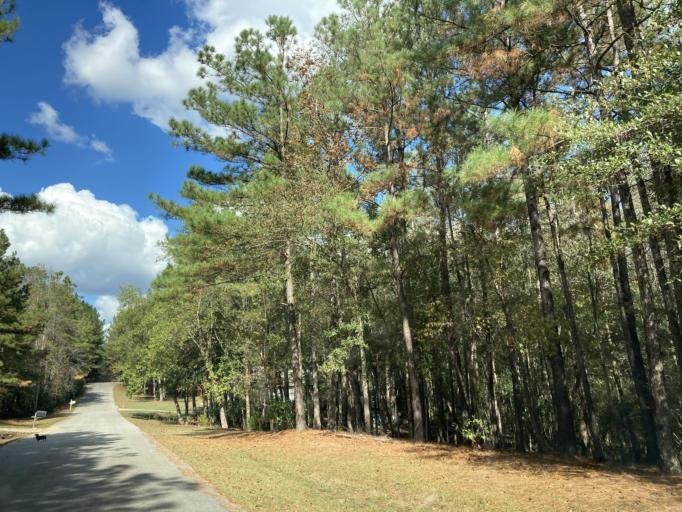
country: US
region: Mississippi
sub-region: Lamar County
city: West Hattiesburg
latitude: 31.2687
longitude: -89.4041
